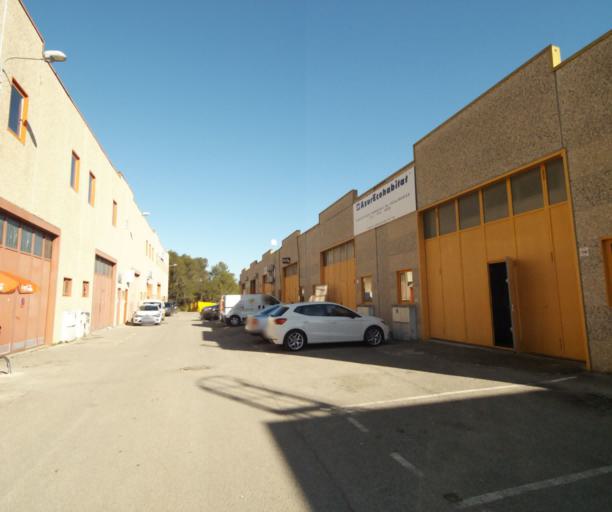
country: FR
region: Provence-Alpes-Cote d'Azur
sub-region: Departement des Alpes-Maritimes
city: Biot
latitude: 43.6094
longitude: 7.0729
